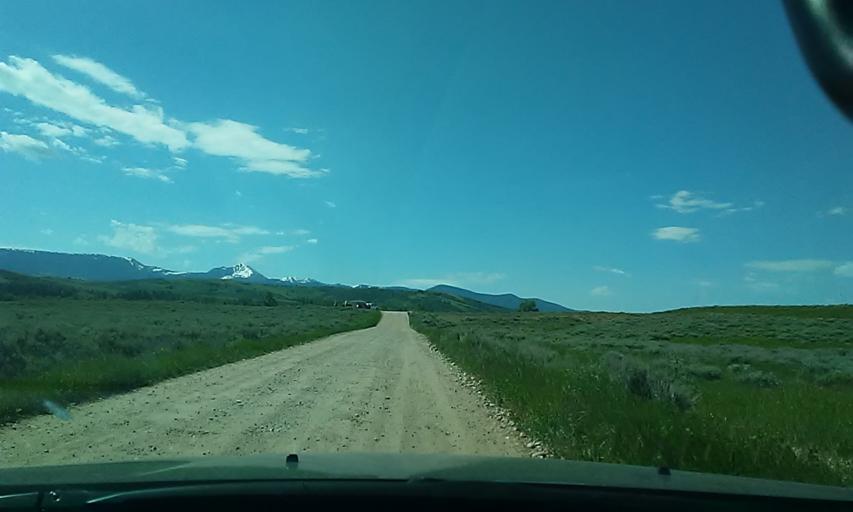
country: US
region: Wyoming
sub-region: Teton County
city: Jackson
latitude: 43.6279
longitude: -110.6642
